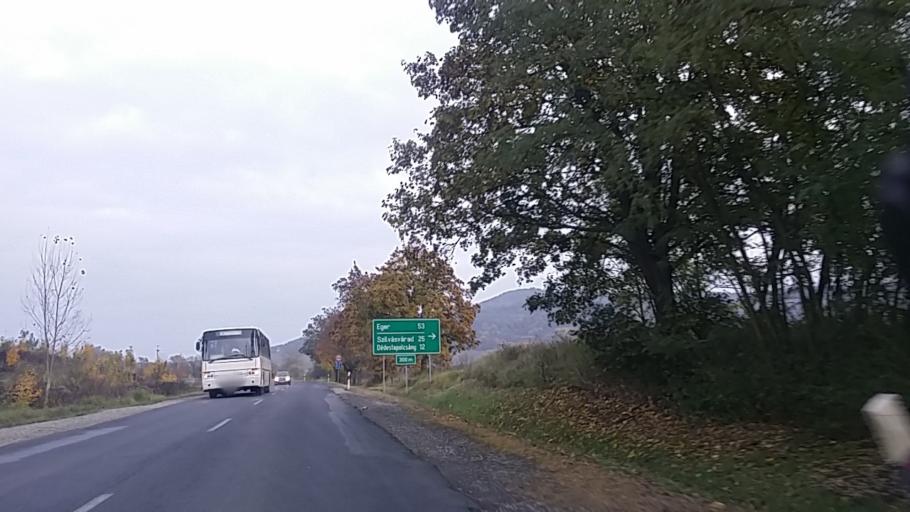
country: HU
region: Borsod-Abauj-Zemplen
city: Sajokaza
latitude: 48.2702
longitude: 20.5386
